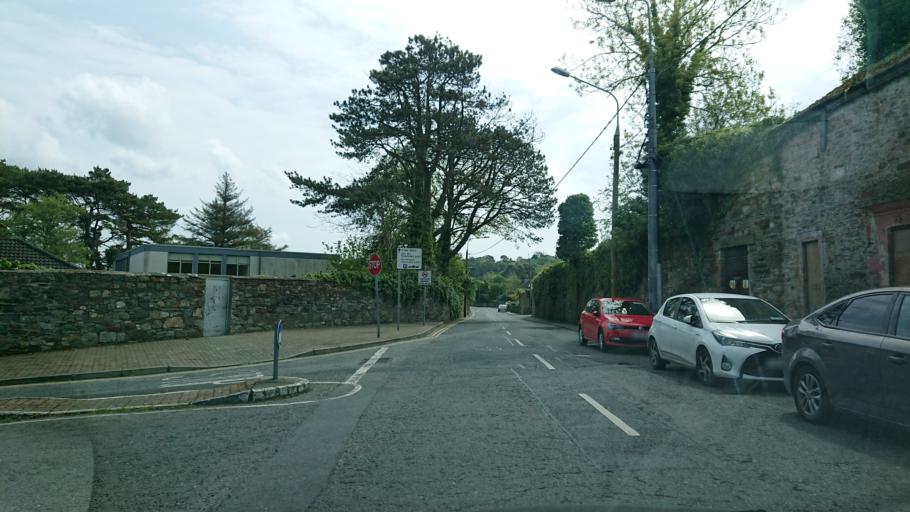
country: IE
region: Munster
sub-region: Waterford
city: Waterford
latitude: 52.2509
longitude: -7.1024
